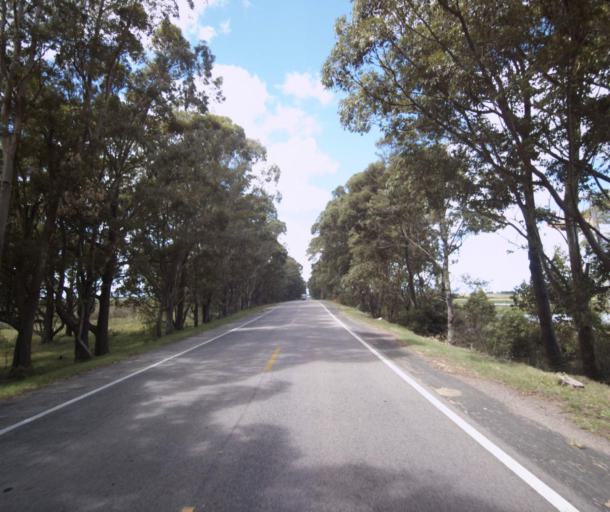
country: BR
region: Rio Grande do Sul
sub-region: Arroio Grande
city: Arroio Grande
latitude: -32.5197
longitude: -52.5536
